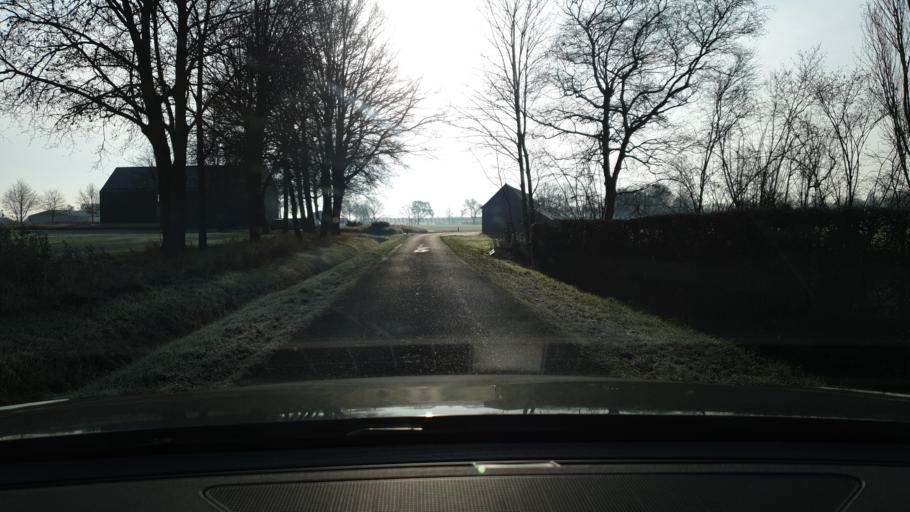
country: NL
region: Limburg
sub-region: Gemeente Peel en Maas
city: Maasbree
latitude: 51.4306
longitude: 6.0482
